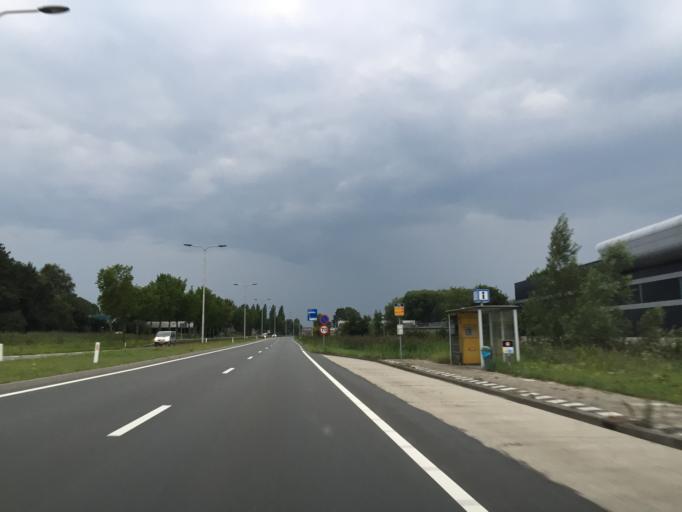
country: NL
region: North Holland
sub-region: Gemeente Aalsmeer
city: Aalsmeer
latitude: 52.2924
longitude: 4.7902
